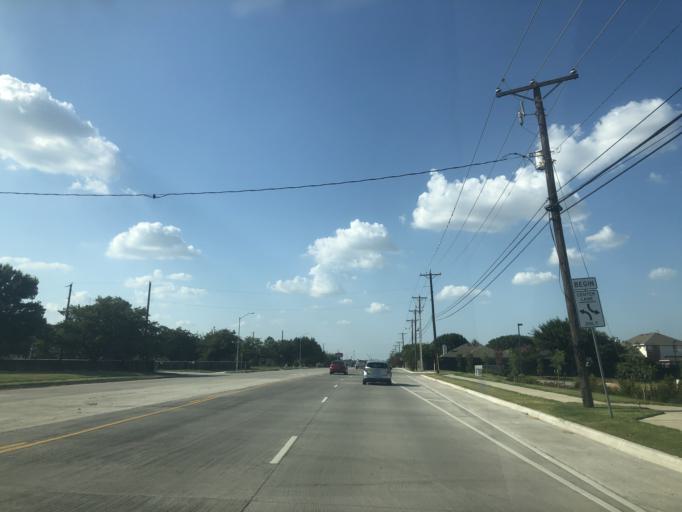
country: US
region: Texas
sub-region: Tarrant County
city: Saginaw
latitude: 32.8653
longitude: -97.3907
